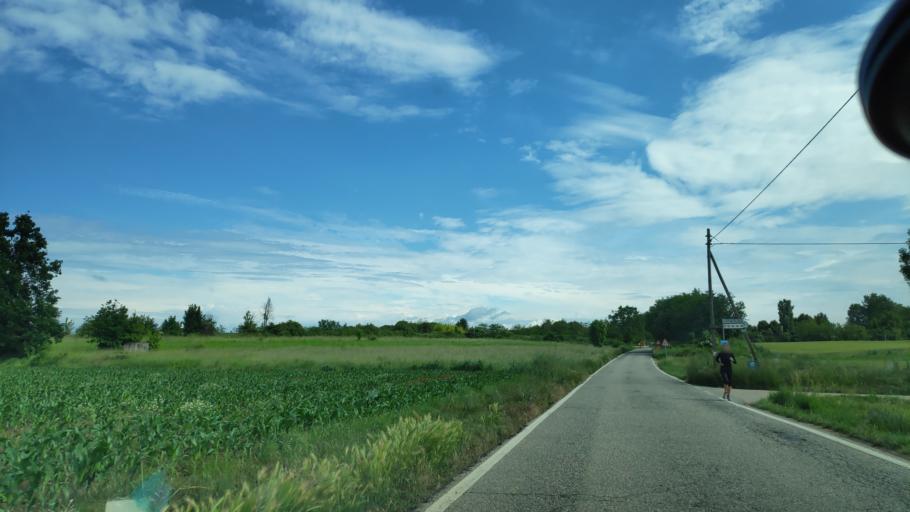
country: IT
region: Piedmont
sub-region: Provincia di Torino
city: Cambiano
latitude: 44.9942
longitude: 7.7738
